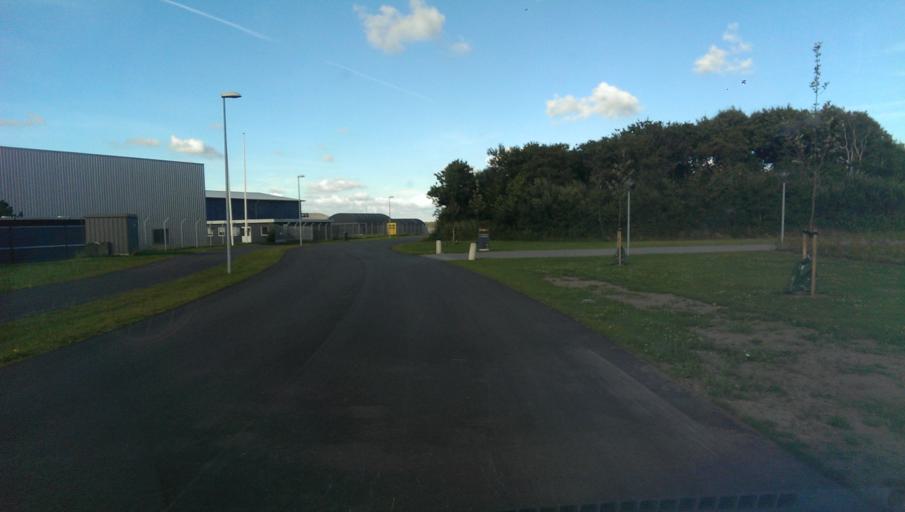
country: DK
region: South Denmark
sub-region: Esbjerg Kommune
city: Tjaereborg
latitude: 55.5219
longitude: 8.5548
